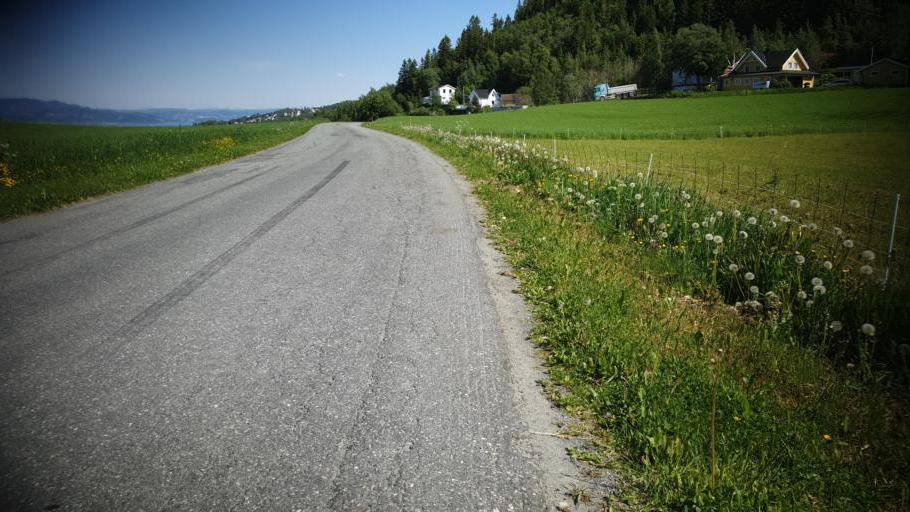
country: NO
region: Sor-Trondelag
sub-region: Malvik
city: Malvik
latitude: 63.4320
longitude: 10.5926
